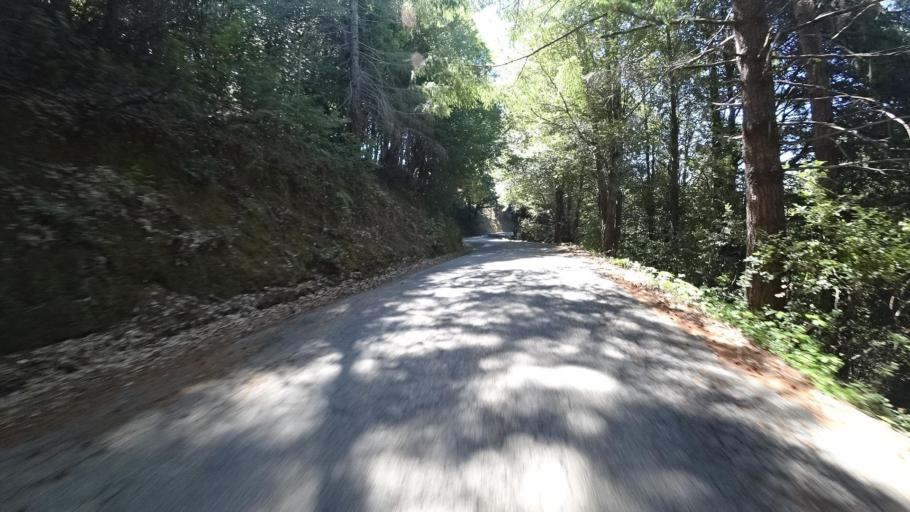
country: US
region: California
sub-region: Humboldt County
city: Redway
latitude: 40.1228
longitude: -123.9698
